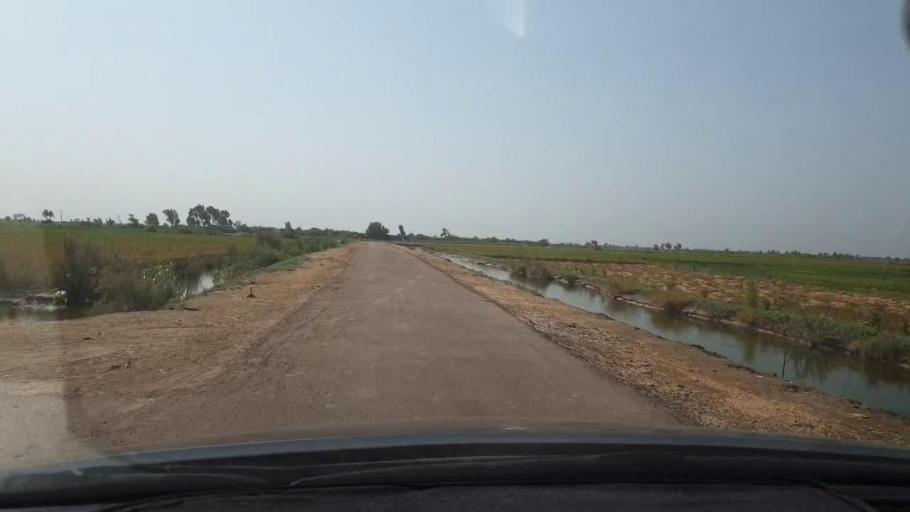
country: PK
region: Sindh
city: Tando Bago
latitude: 24.7023
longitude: 69.1071
